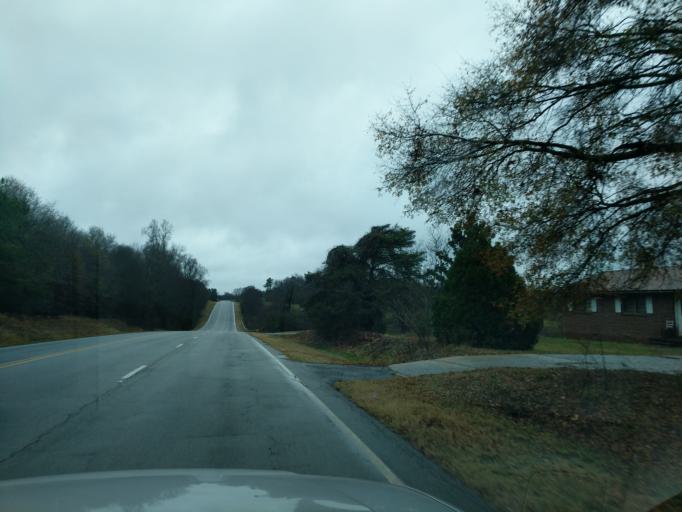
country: US
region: Georgia
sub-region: Hart County
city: Royston
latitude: 34.3287
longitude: -83.1099
